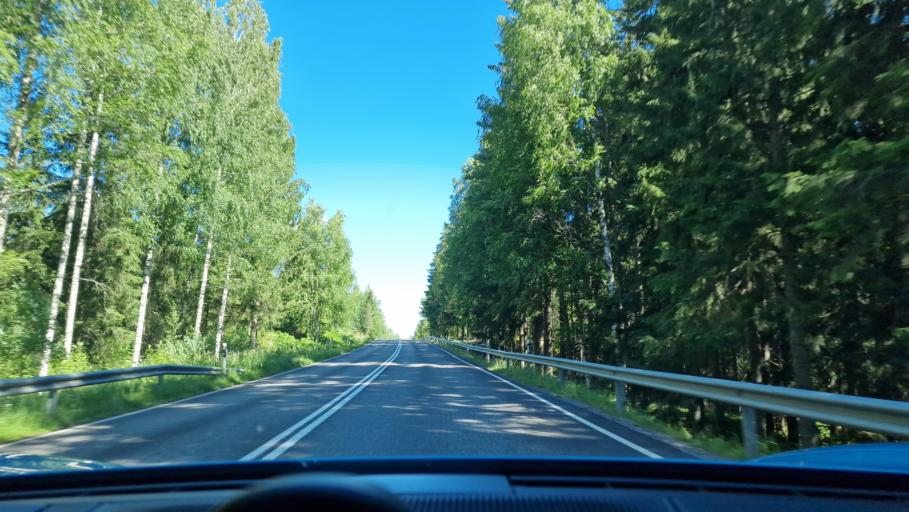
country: FI
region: Pirkanmaa
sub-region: Tampere
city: Orivesi
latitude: 61.5968
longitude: 24.3114
